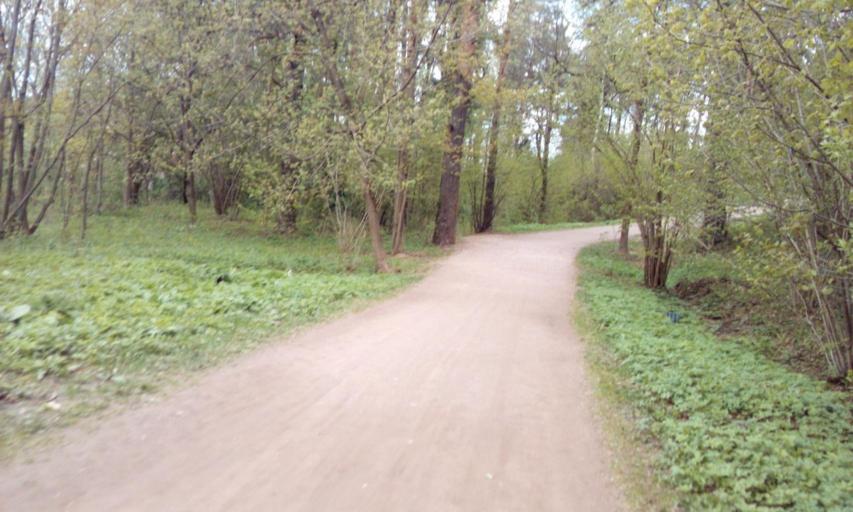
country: RU
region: Moskovskaya
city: Skolkovo
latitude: 55.6721
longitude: 37.3490
